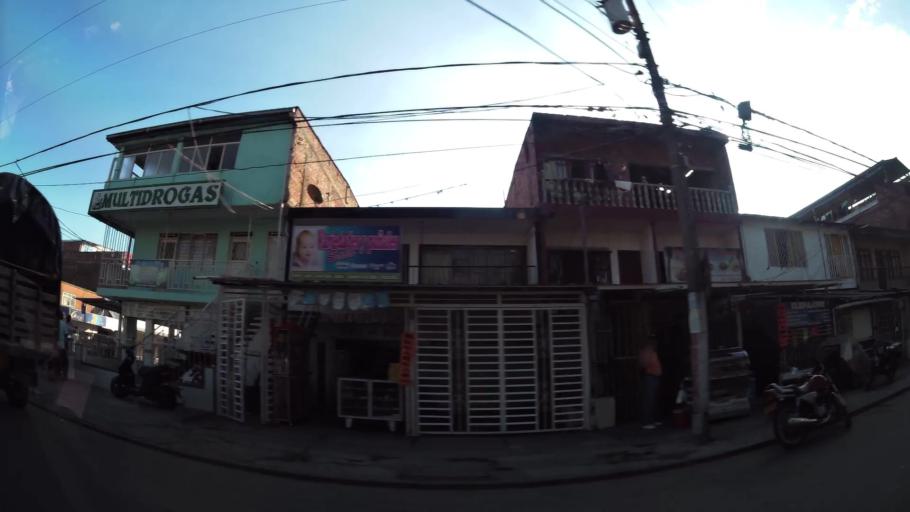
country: CO
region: Valle del Cauca
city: Cali
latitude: 3.4096
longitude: -76.5056
